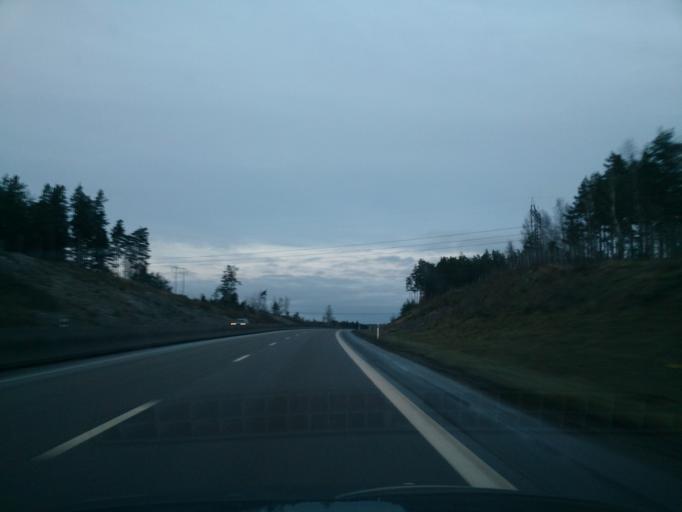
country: SE
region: OEstergoetland
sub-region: Norrkopings Kommun
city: Kimstad
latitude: 58.5136
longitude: 15.9945
